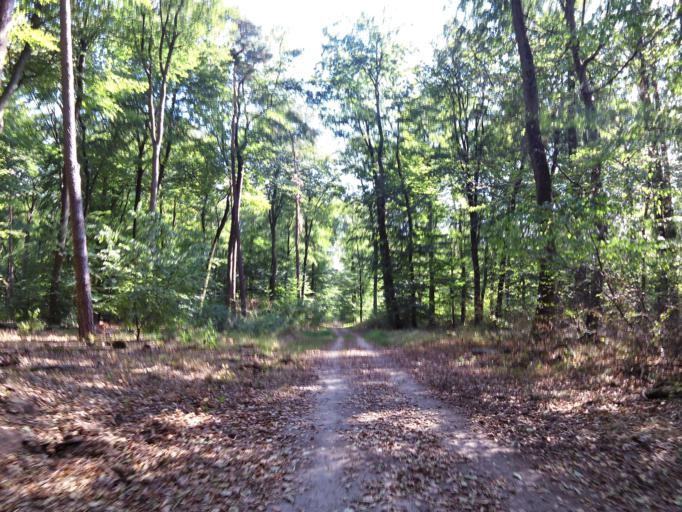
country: DE
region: Hesse
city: Morfelden-Walldorf
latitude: 50.0188
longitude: 8.5673
